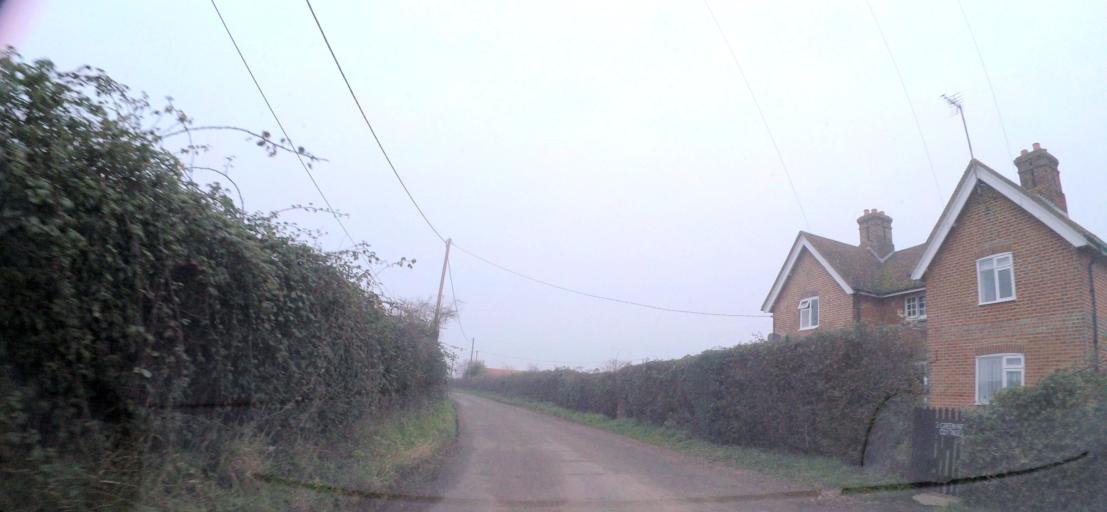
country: GB
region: England
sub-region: West Berkshire
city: Theale
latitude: 51.4086
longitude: -1.0999
